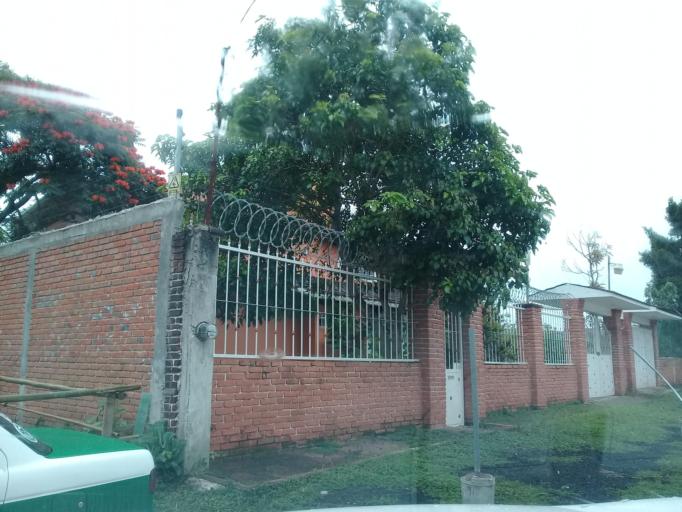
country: MX
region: Veracruz
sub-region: Emiliano Zapata
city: Jacarandas
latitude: 19.5035
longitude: -96.8445
